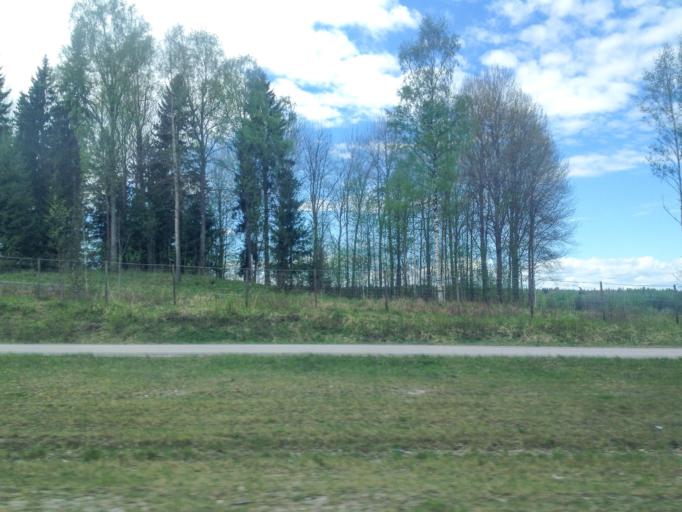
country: FI
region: Uusimaa
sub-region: Helsinki
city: Hyvinge
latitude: 60.6396
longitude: 24.8092
